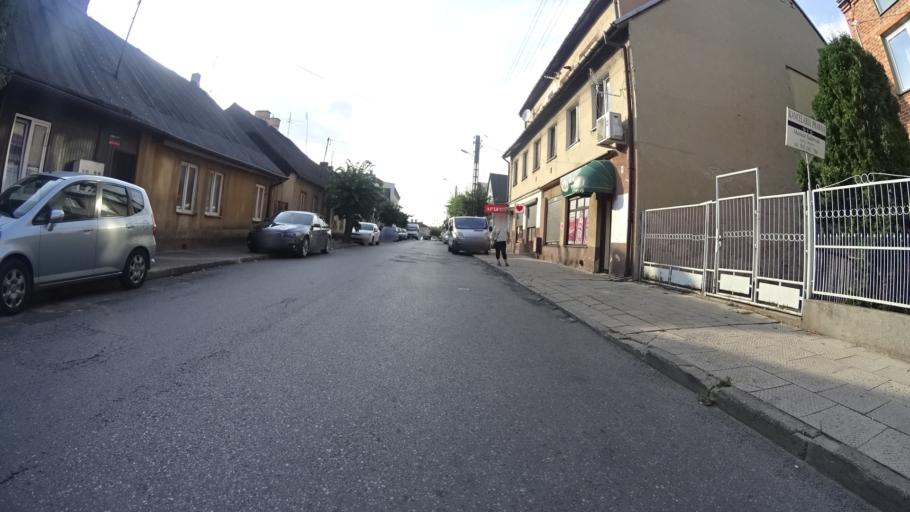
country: PL
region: Masovian Voivodeship
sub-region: Powiat grojecki
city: Mogielnica
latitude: 51.6934
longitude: 20.7249
